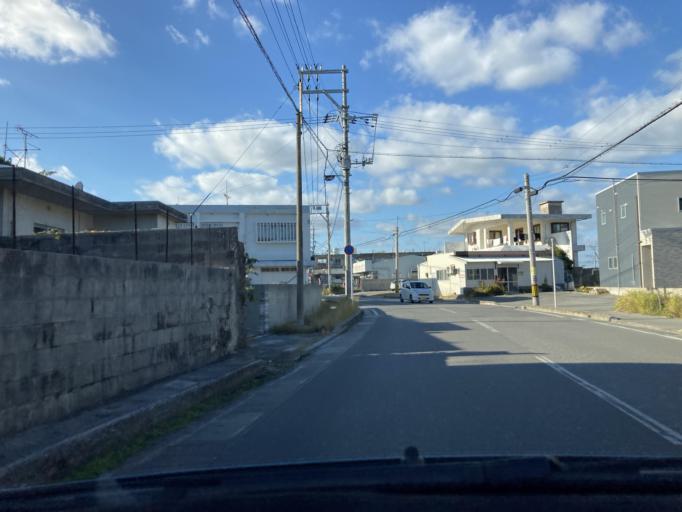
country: JP
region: Okinawa
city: Katsuren-haebaru
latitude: 26.3239
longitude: 127.9064
